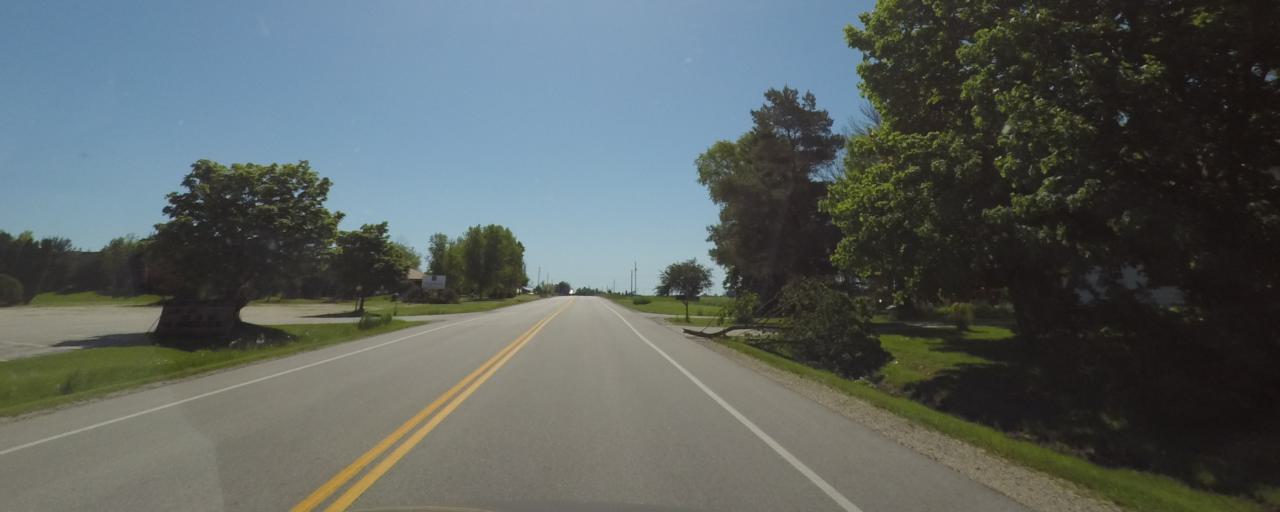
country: US
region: Wisconsin
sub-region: Sheboygan County
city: Sheboygan Falls
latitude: 43.7470
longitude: -87.8870
